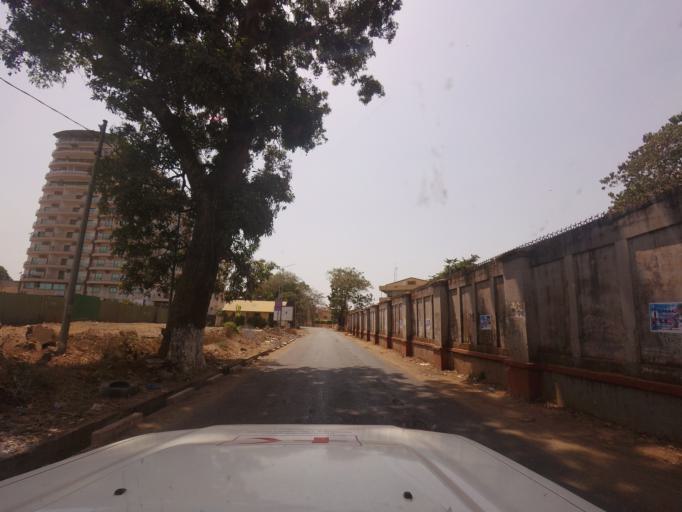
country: GN
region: Conakry
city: Camayenne
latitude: 9.5162
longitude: -13.7117
